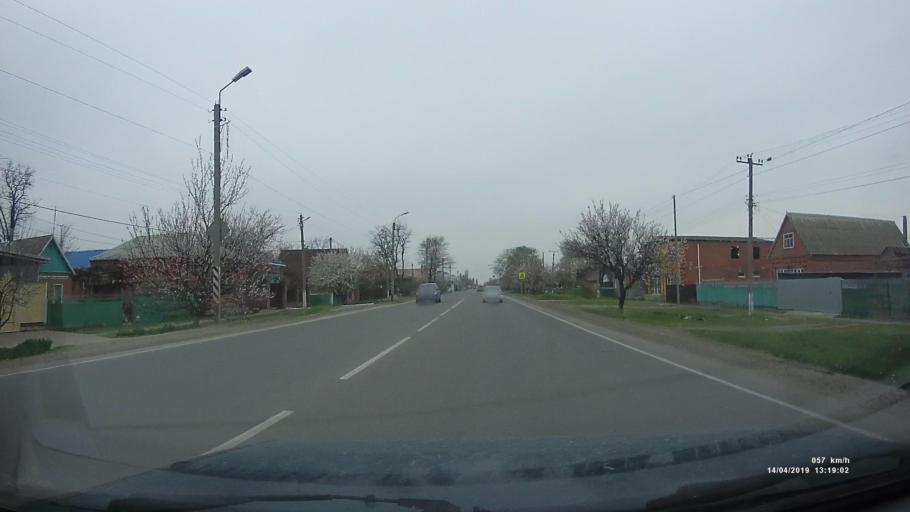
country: RU
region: Rostov
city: Kuleshovka
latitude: 47.0795
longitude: 39.5506
